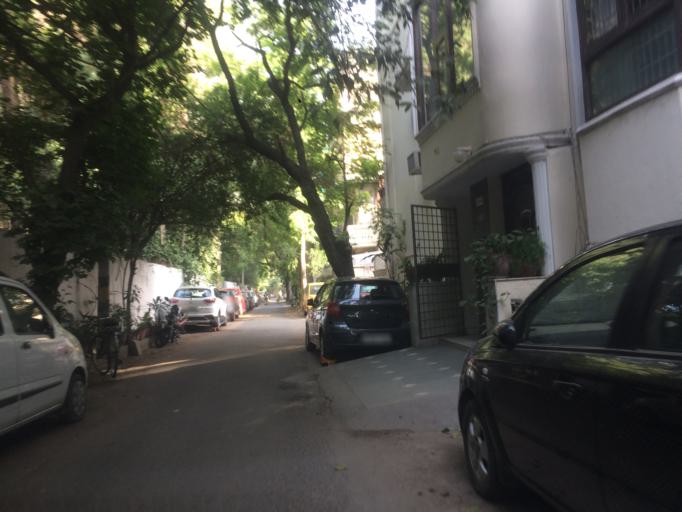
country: IN
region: NCT
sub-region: New Delhi
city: New Delhi
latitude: 28.5469
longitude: 77.2330
